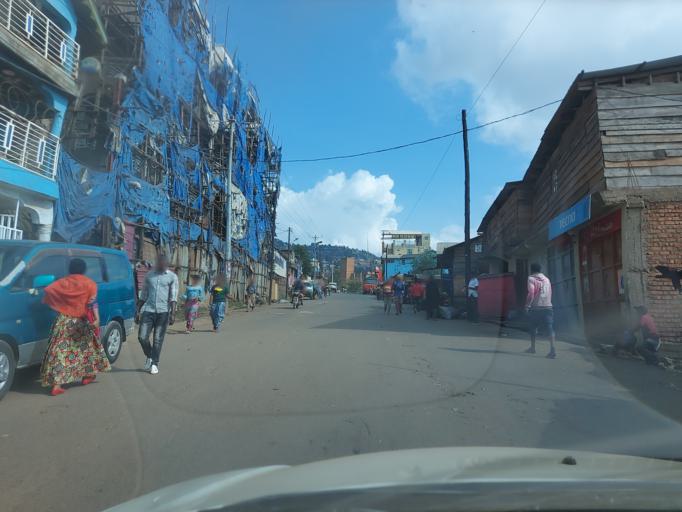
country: CD
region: South Kivu
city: Bukavu
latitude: -2.5199
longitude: 28.8512
